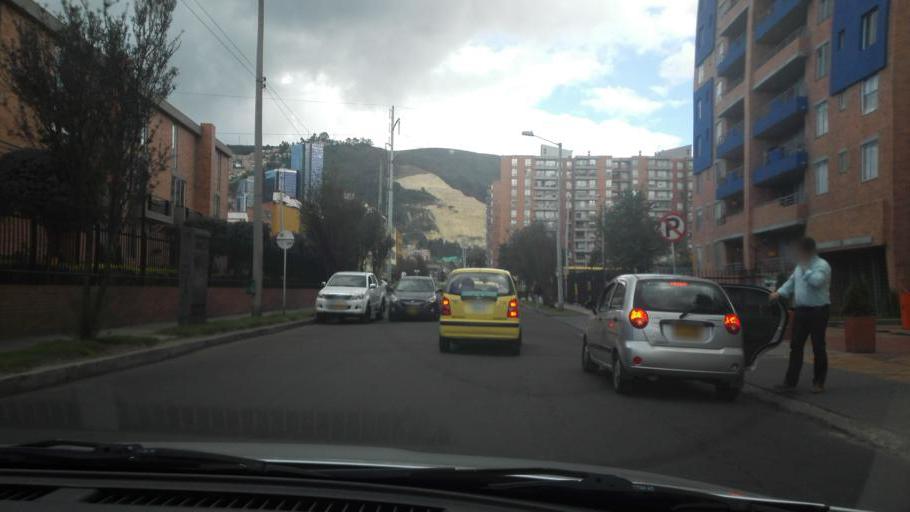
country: CO
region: Cundinamarca
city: La Calera
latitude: 4.7332
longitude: -74.0329
